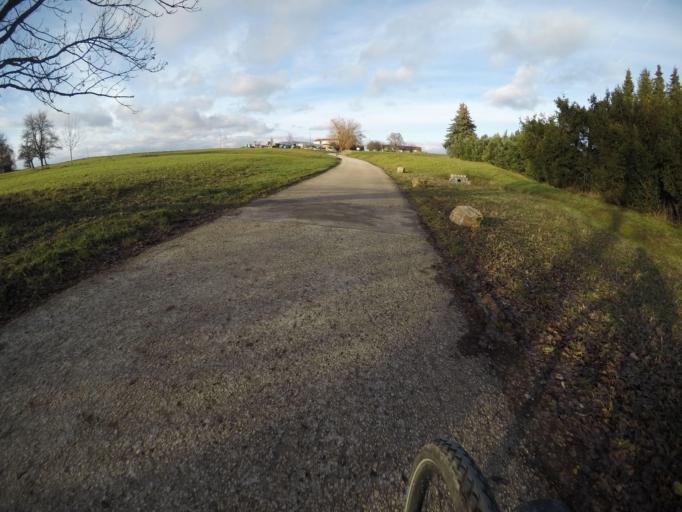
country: DE
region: Baden-Wuerttemberg
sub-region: Regierungsbezirk Stuttgart
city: Filderstadt
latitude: 48.6539
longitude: 9.2457
